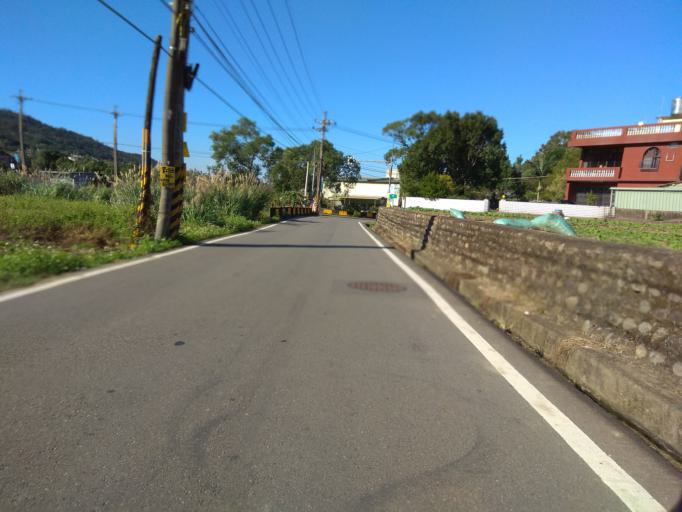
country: TW
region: Taiwan
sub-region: Hsinchu
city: Zhubei
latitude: 24.8442
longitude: 121.1247
